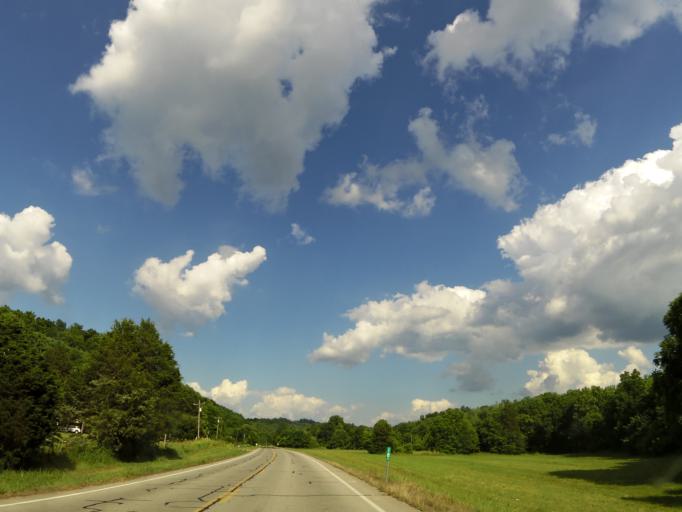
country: US
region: Tennessee
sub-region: Perry County
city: Linden
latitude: 35.6247
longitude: -87.7456
